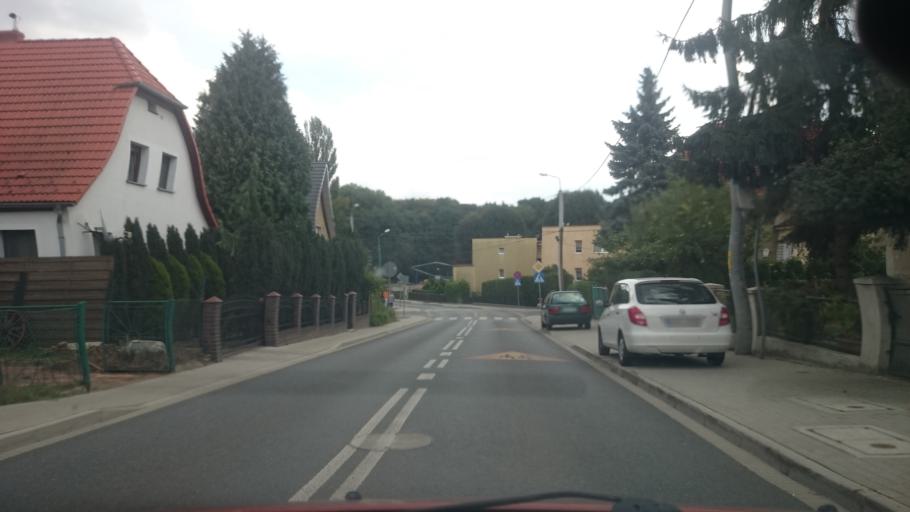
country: PL
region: Lower Silesian Voivodeship
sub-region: Powiat zabkowicki
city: Zabkowice Slaskie
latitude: 50.5935
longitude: 16.8188
